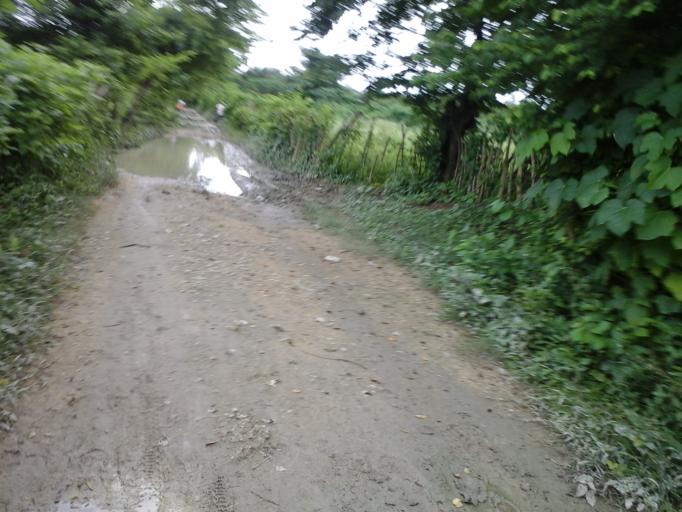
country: CO
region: Bolivar
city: San Pablo
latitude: 10.1556
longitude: -75.2739
